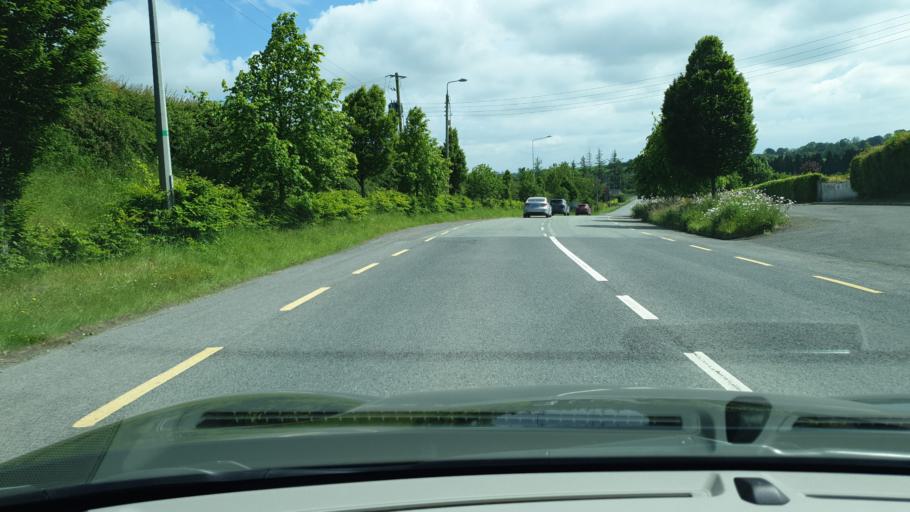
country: IE
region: Ulster
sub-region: An Cabhan
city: Kingscourt
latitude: 53.8185
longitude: -6.7415
